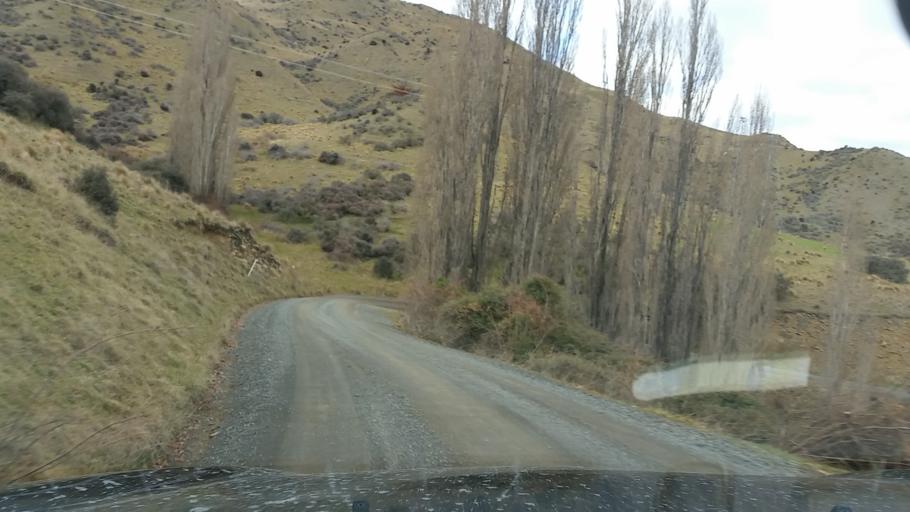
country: NZ
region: Marlborough
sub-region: Marlborough District
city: Blenheim
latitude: -41.8932
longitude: 173.6138
